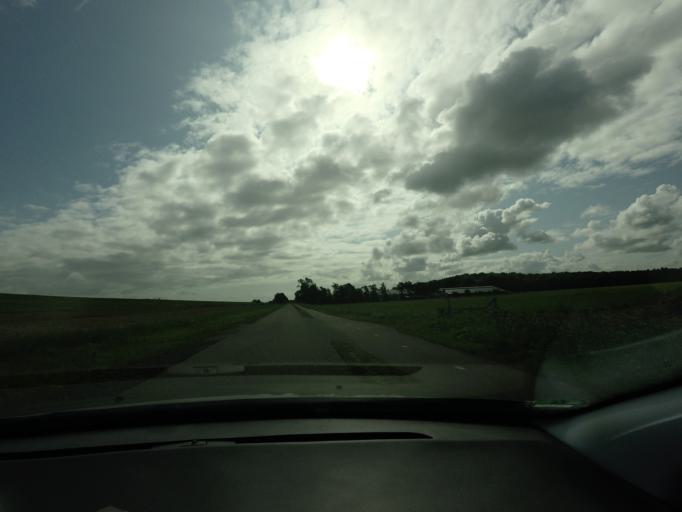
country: NL
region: North Holland
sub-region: Gemeente Hollands Kroon
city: Den Oever
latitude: 52.8994
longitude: 5.0676
